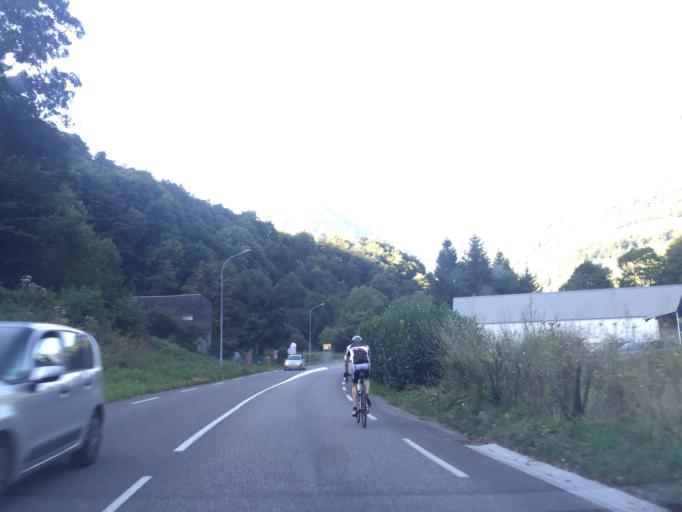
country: FR
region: Midi-Pyrenees
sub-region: Departement des Hautes-Pyrenees
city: Cauterets
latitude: 42.9086
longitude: -0.1013
